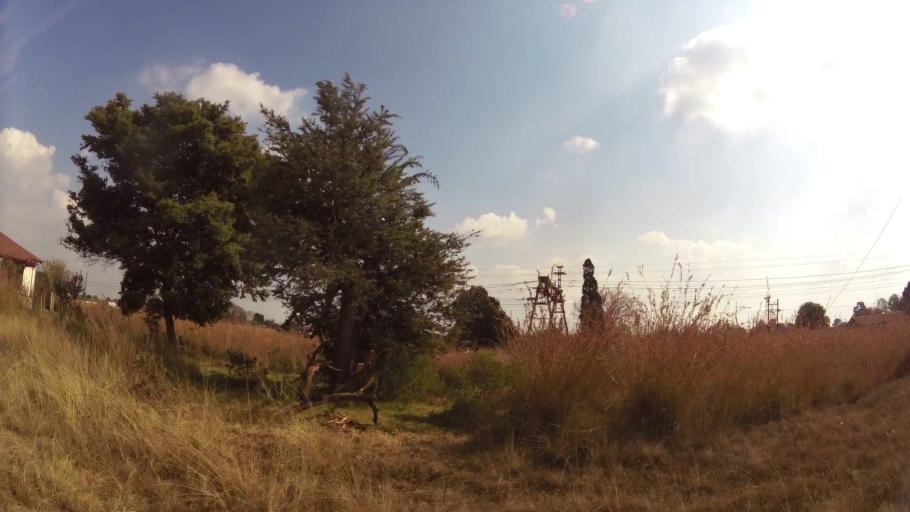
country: ZA
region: Mpumalanga
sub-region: Nkangala District Municipality
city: Delmas
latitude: -26.1910
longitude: 28.5395
